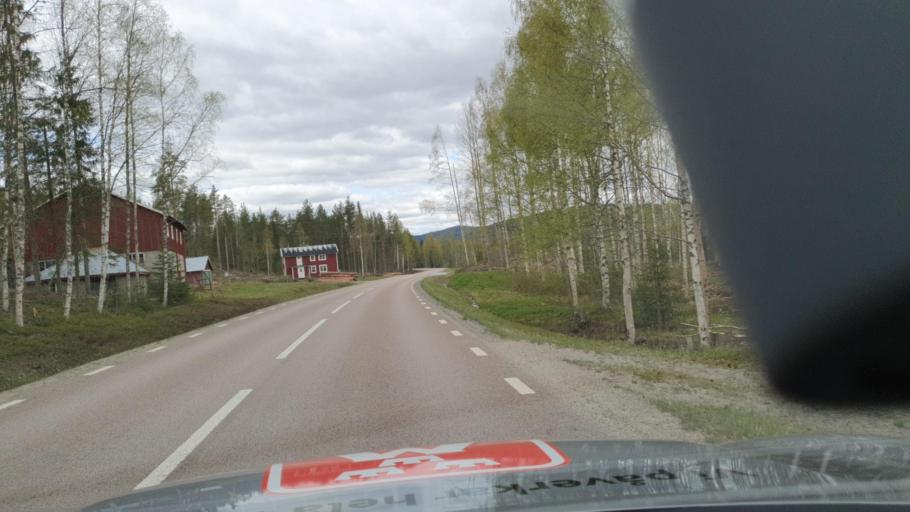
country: SE
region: Vaesternorrland
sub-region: OErnskoeldsviks Kommun
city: Ornskoldsvik
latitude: 63.5004
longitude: 18.8542
